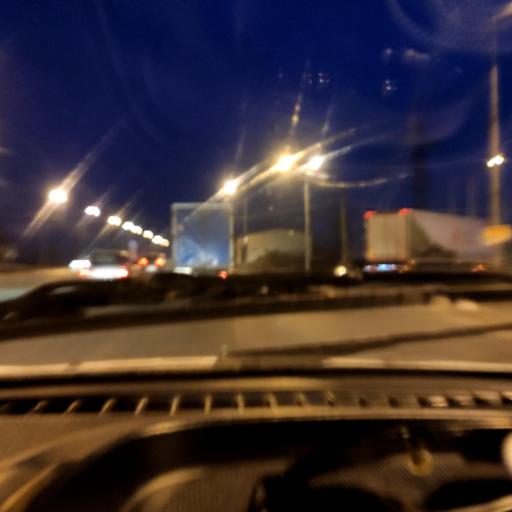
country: RU
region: Samara
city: Zhigulevsk
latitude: 53.5418
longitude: 49.5147
